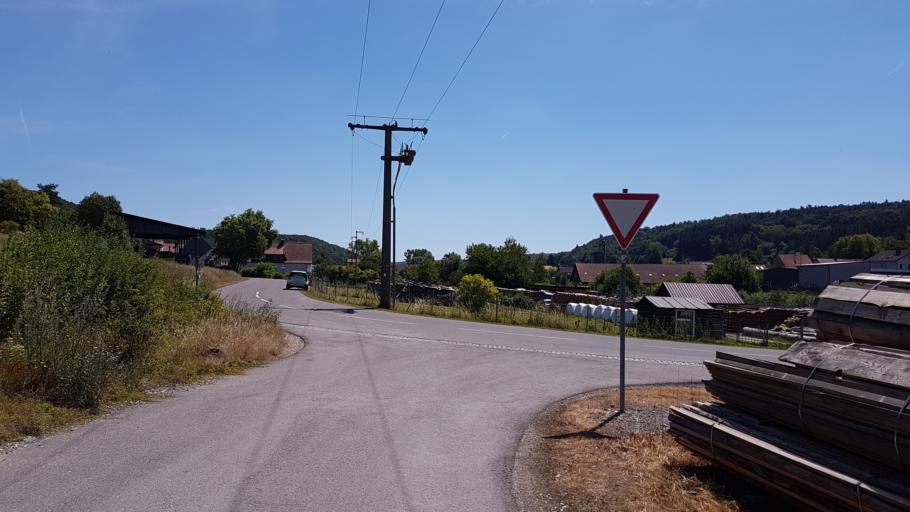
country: DE
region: Bavaria
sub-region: Regierungsbezirk Unterfranken
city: Sand
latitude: 49.9528
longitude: 10.5918
